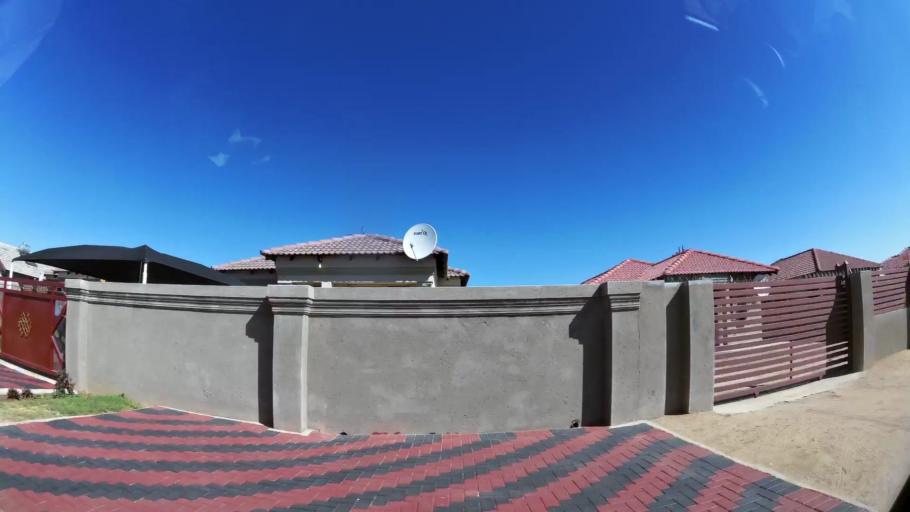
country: ZA
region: Limpopo
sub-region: Capricorn District Municipality
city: Polokwane
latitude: -23.8642
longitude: 29.4244
